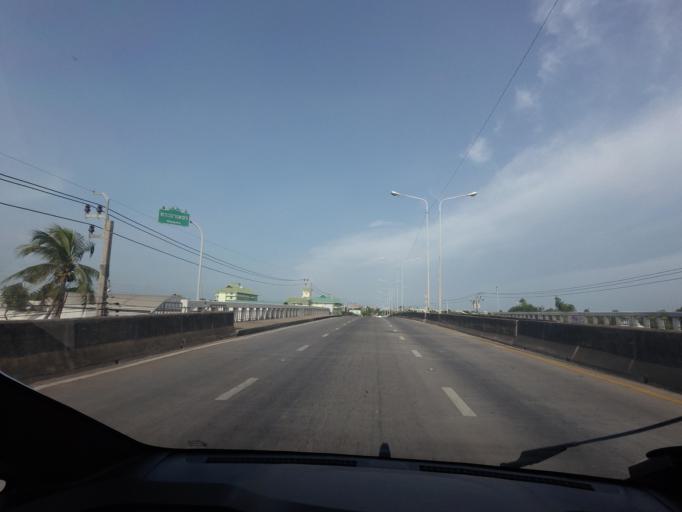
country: TH
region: Samut Prakan
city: Ban Khlong Bang Sao Thong
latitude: 13.7024
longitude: 100.8428
